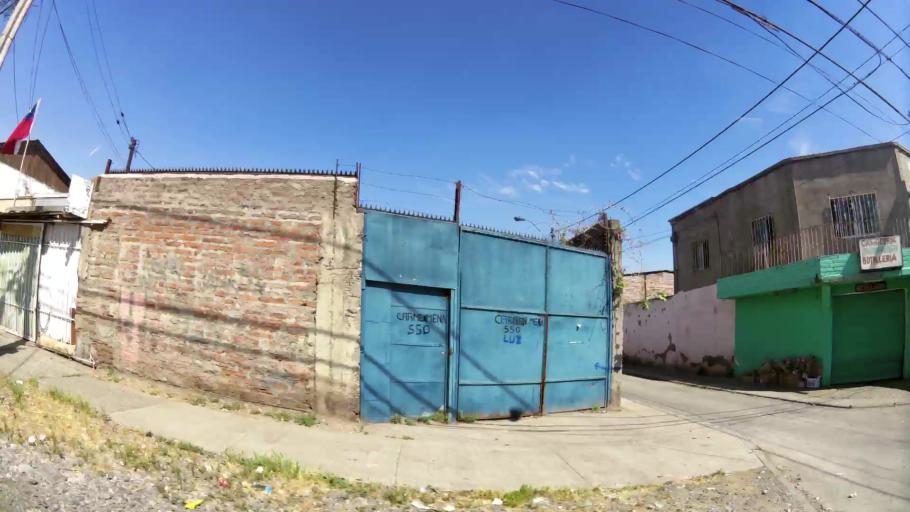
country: CL
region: Santiago Metropolitan
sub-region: Provincia de Santiago
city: Santiago
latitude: -33.5090
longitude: -70.6407
